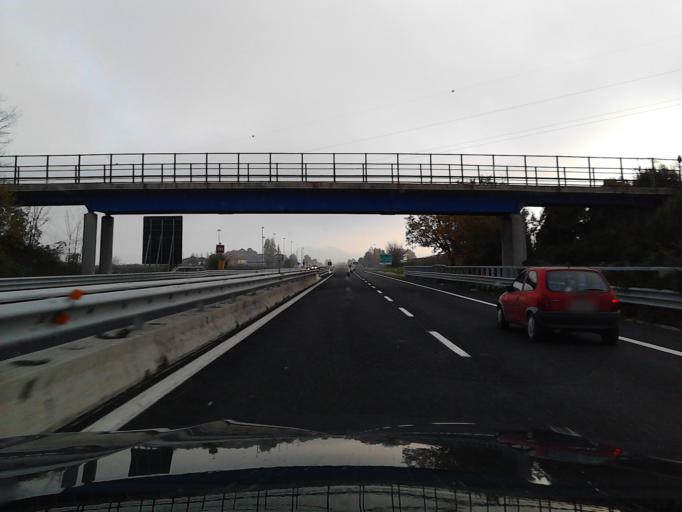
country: IT
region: Abruzzo
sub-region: Provincia di Chieti
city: Francavilla al Mare
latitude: 42.3917
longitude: 14.2887
